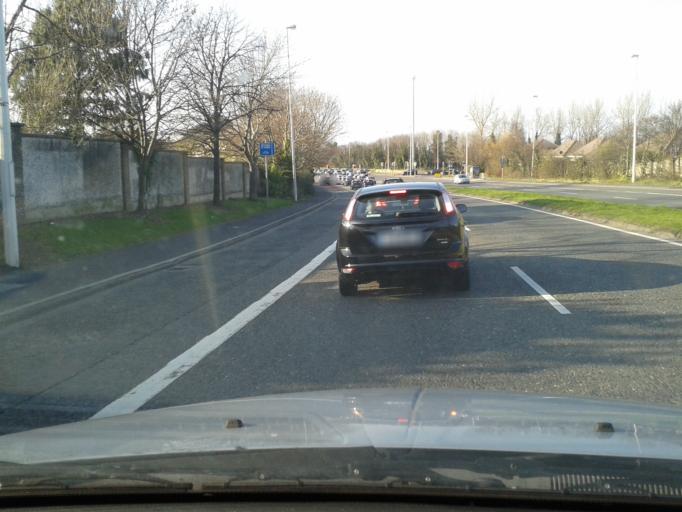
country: IE
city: Booterstown
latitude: 53.2879
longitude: -6.1947
